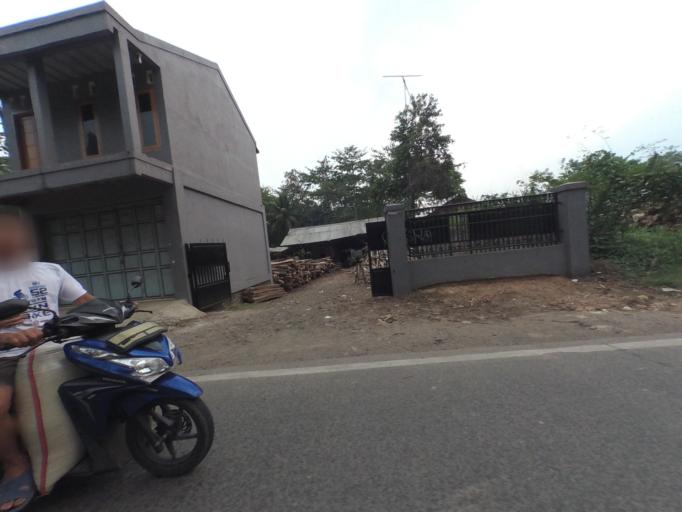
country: ID
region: West Java
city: Sidoger Lebak
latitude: -6.5651
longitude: 106.5896
